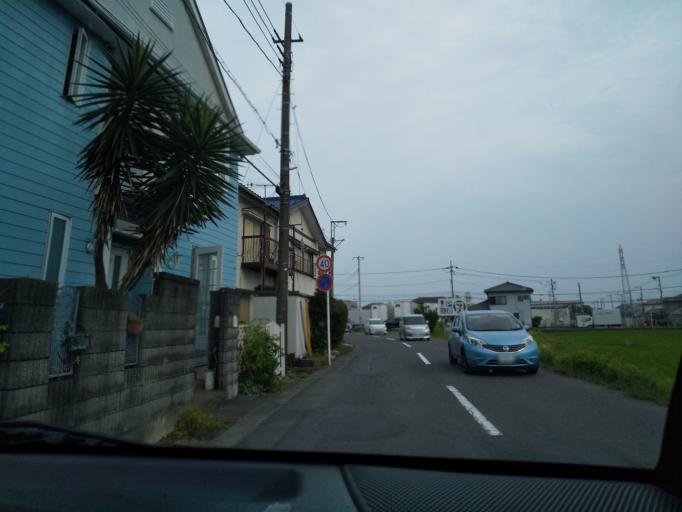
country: JP
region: Kanagawa
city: Atsugi
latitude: 35.3936
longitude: 139.3852
